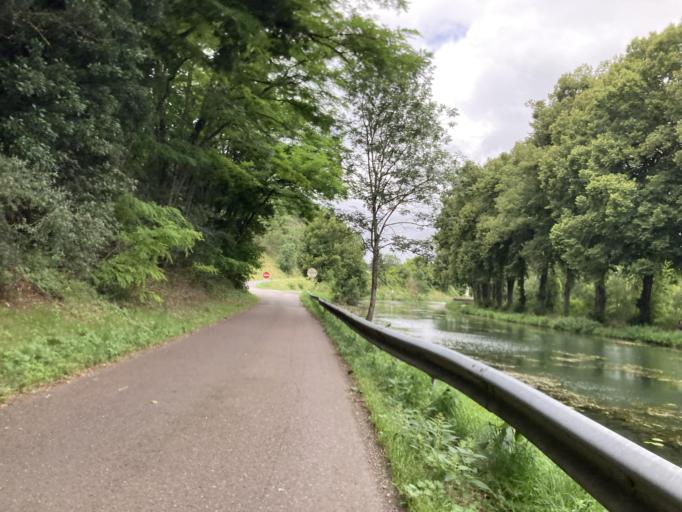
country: FR
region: Bourgogne
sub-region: Departement de la Cote-d'Or
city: Plombieres-les-Dijon
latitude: 47.3306
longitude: 4.9820
